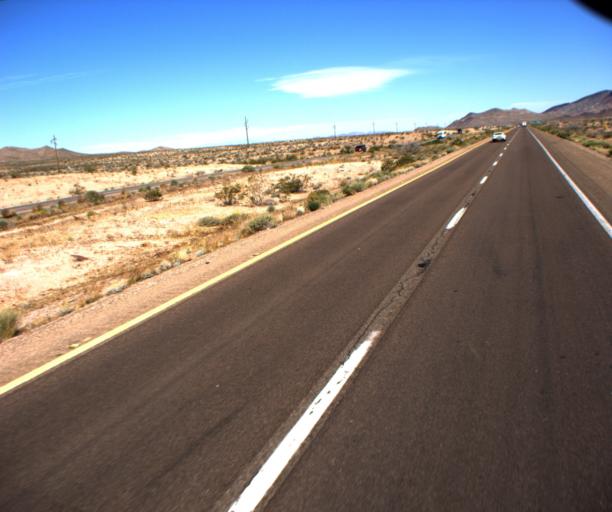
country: US
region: Nevada
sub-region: Clark County
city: Boulder City
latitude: 35.8151
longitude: -114.5479
